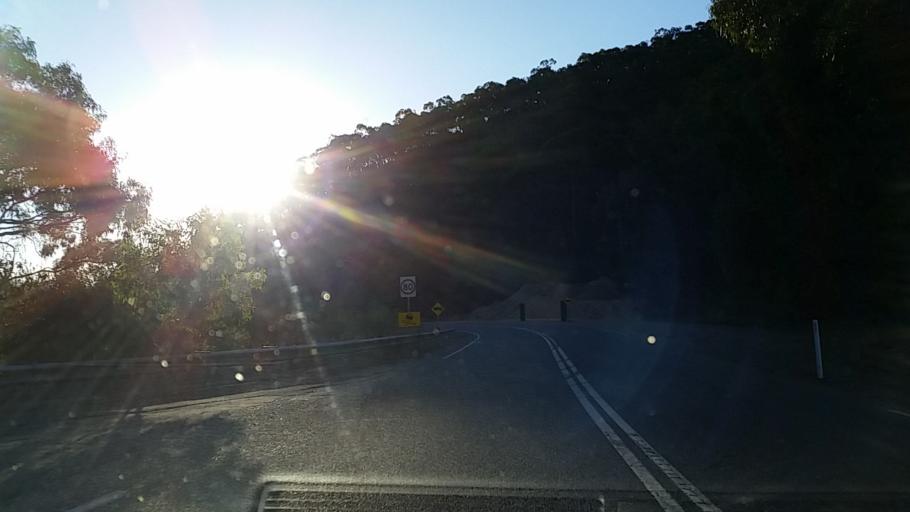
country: AU
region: South Australia
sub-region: Campbelltown
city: Athelstone
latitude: -34.8643
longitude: 138.7784
